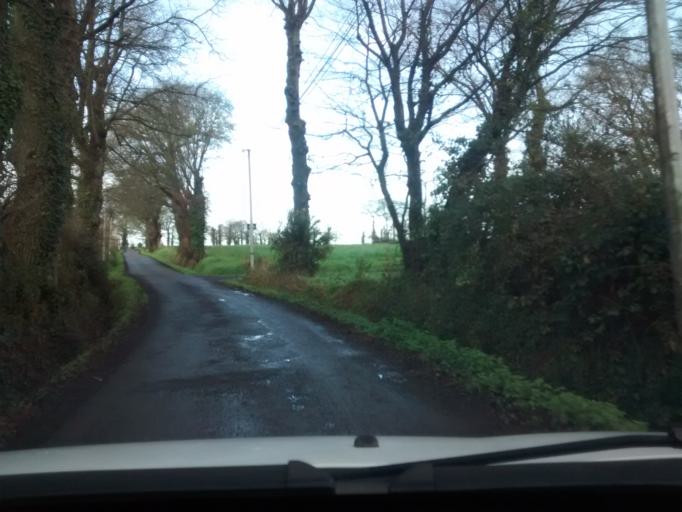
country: FR
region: Brittany
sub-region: Departement d'Ille-et-Vilaine
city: Montgermont
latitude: 48.1295
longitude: -1.7140
